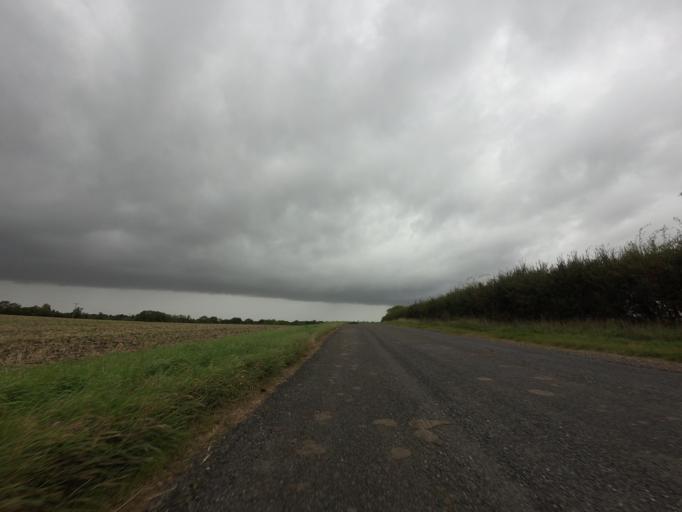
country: GB
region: England
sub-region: Cambridgeshire
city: Wimpole
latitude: 52.1823
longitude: -0.0418
